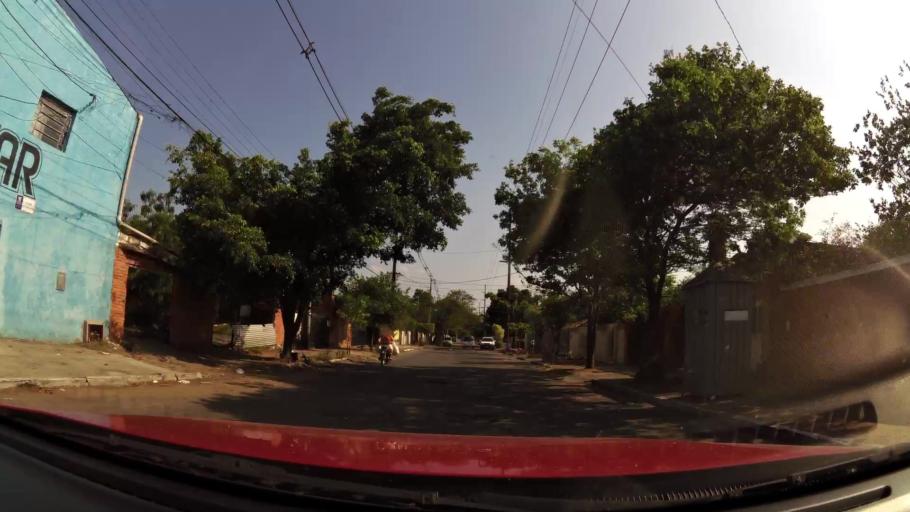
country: PY
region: Asuncion
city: Asuncion
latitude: -25.3159
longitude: -57.6340
